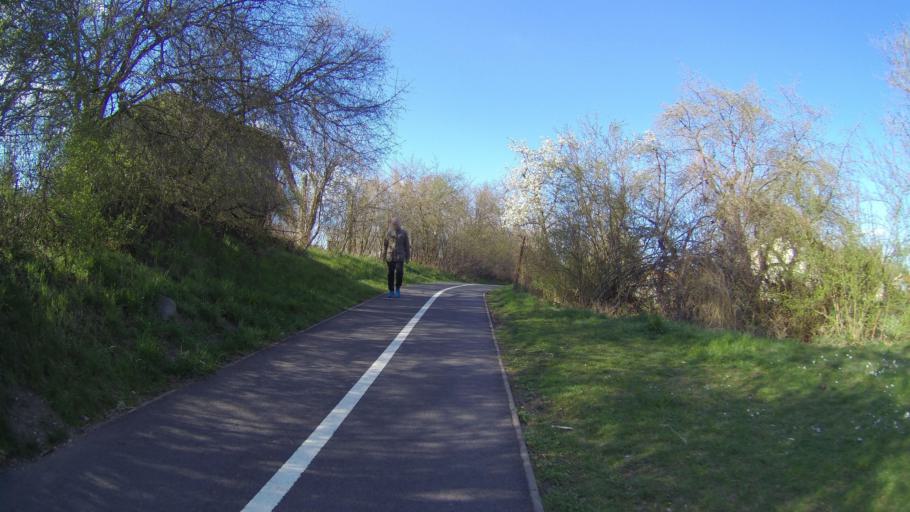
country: CZ
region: Ustecky
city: Zatec
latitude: 50.3330
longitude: 13.5346
